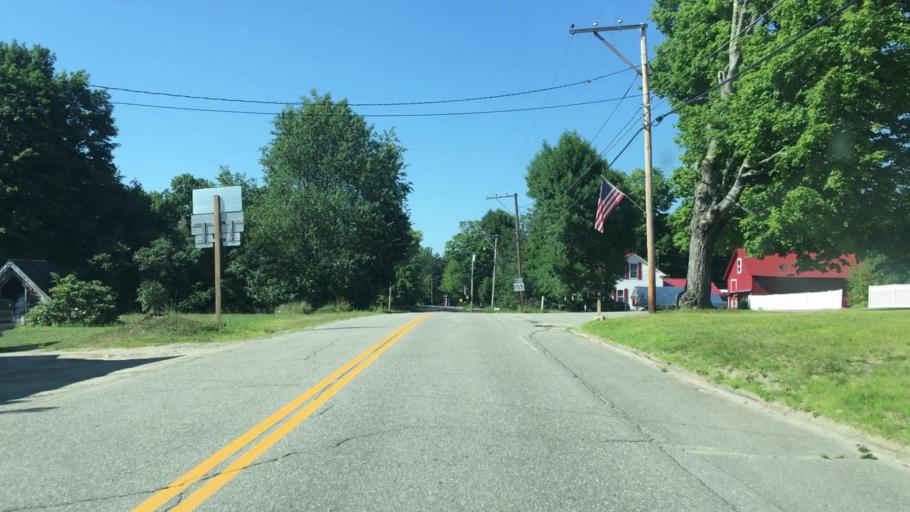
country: US
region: Maine
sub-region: Penobscot County
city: Enfield
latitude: 45.2491
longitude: -68.5658
